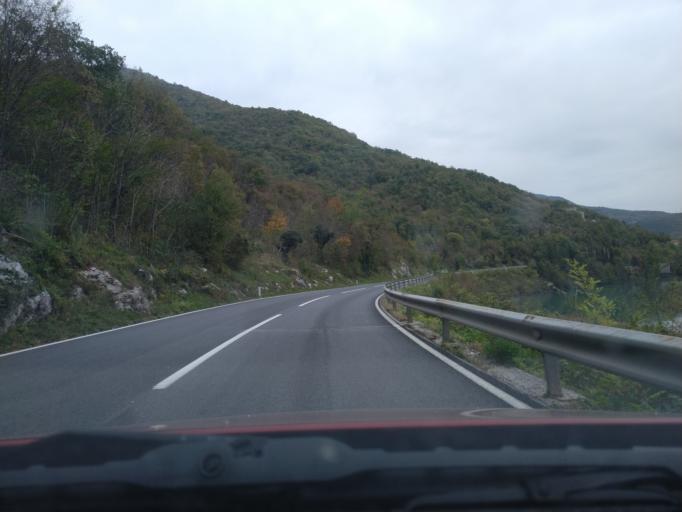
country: SI
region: Nova Gorica
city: Solkan
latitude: 45.9983
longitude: 13.6360
